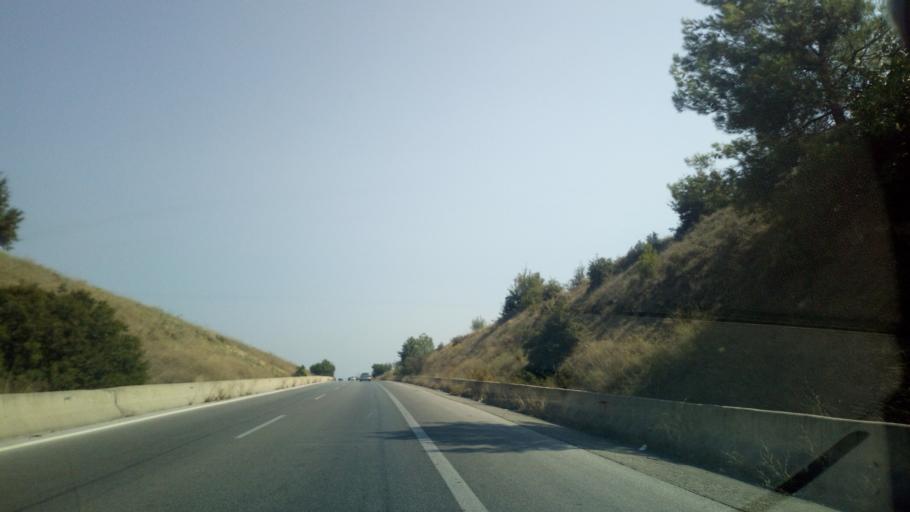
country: GR
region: Central Macedonia
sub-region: Nomos Chalkidikis
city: Nea Kallikrateia
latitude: 40.3303
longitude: 23.0766
